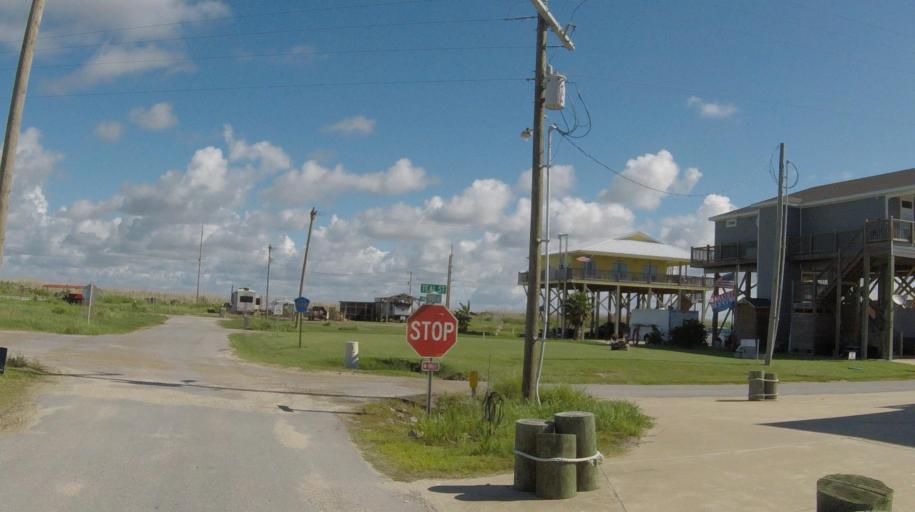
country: US
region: Louisiana
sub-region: Cameron Parish
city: Cameron
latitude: 29.7709
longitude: -93.4593
